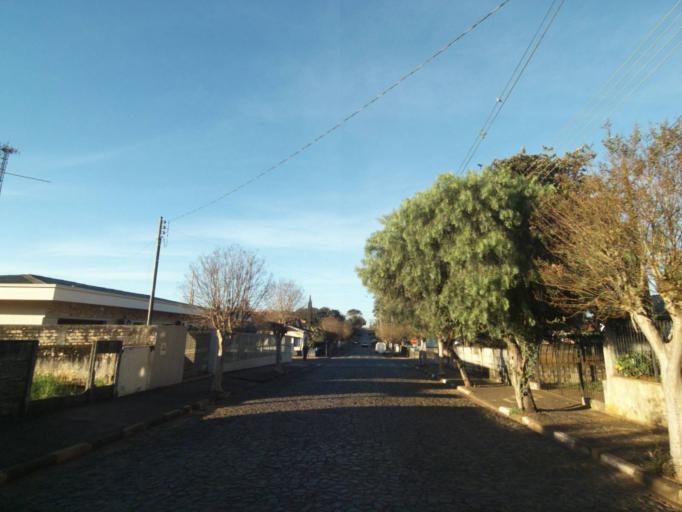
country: BR
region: Parana
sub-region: Tibagi
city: Tibagi
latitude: -24.5179
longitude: -50.4123
